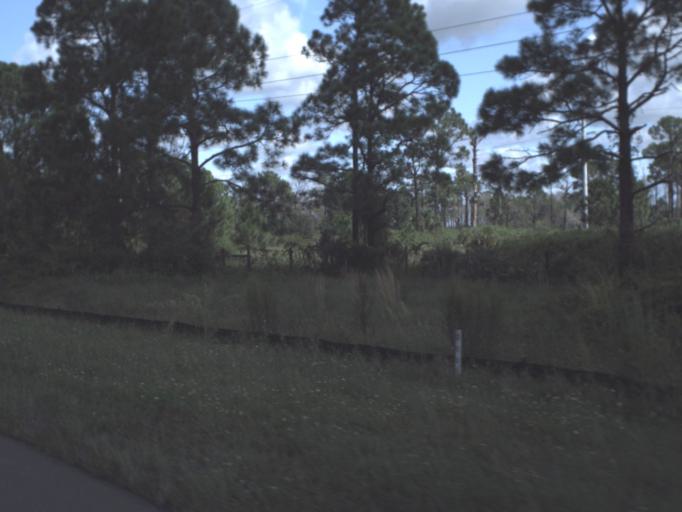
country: US
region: Florida
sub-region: Charlotte County
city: Port Charlotte
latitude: 27.0696
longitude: -82.0955
